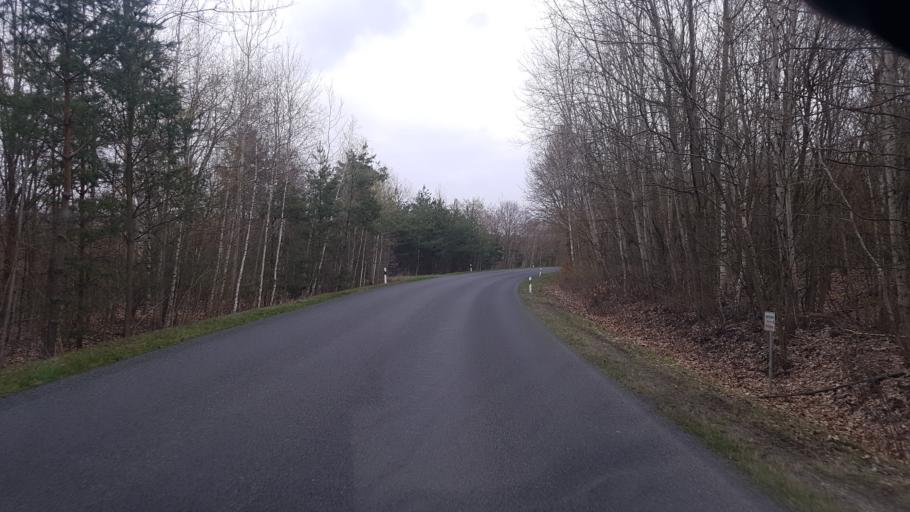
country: DE
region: Brandenburg
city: Lauchhammer
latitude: 51.4901
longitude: 13.7942
